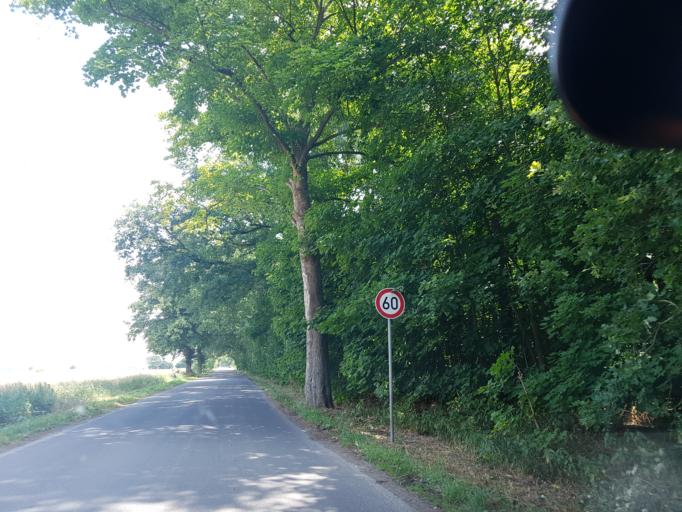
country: DE
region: Brandenburg
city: Stahnsdorf
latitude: 52.3658
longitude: 13.2126
